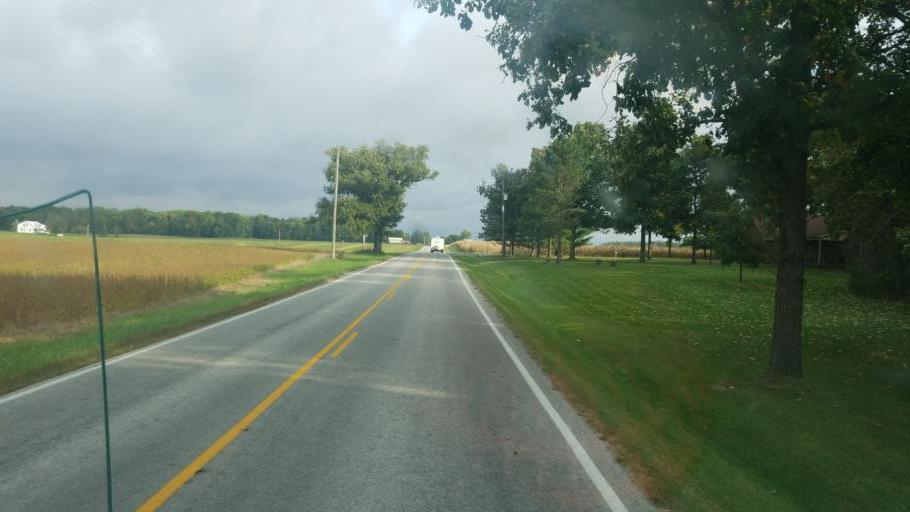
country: US
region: Ohio
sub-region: Seneca County
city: Fostoria
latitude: 41.0495
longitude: -83.4772
